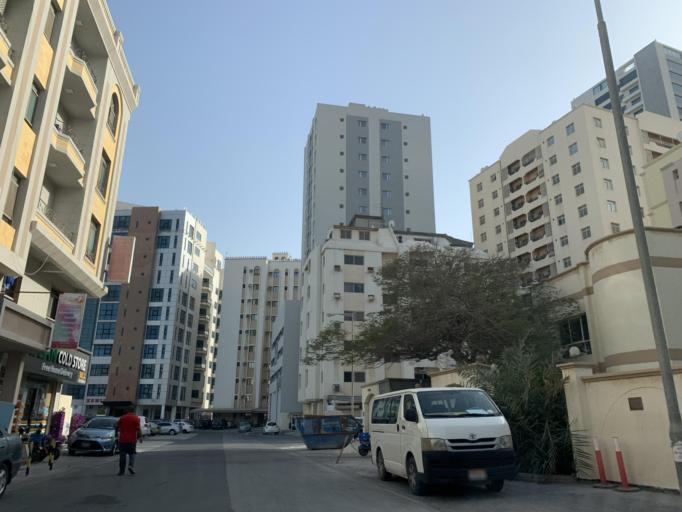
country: BH
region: Manama
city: Manama
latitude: 26.2051
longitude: 50.5814
